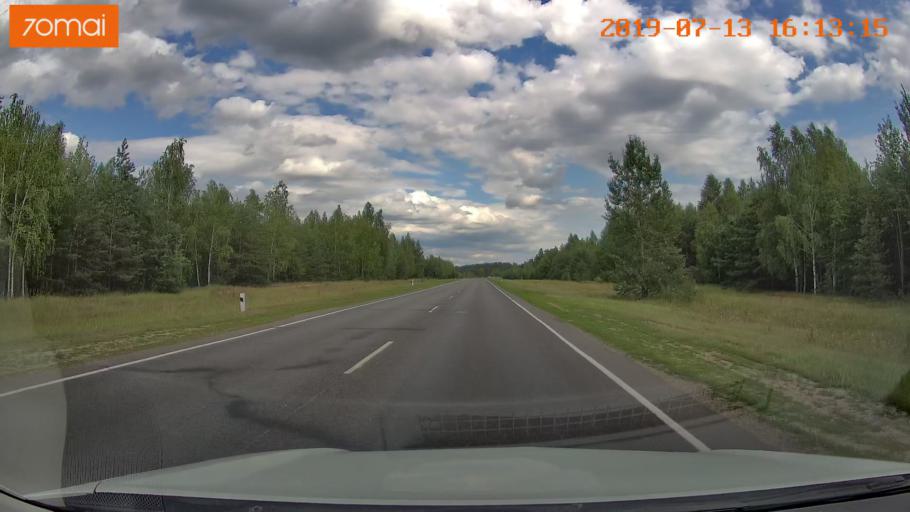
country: BY
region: Mogilev
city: Babruysk
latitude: 53.1637
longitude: 29.2989
